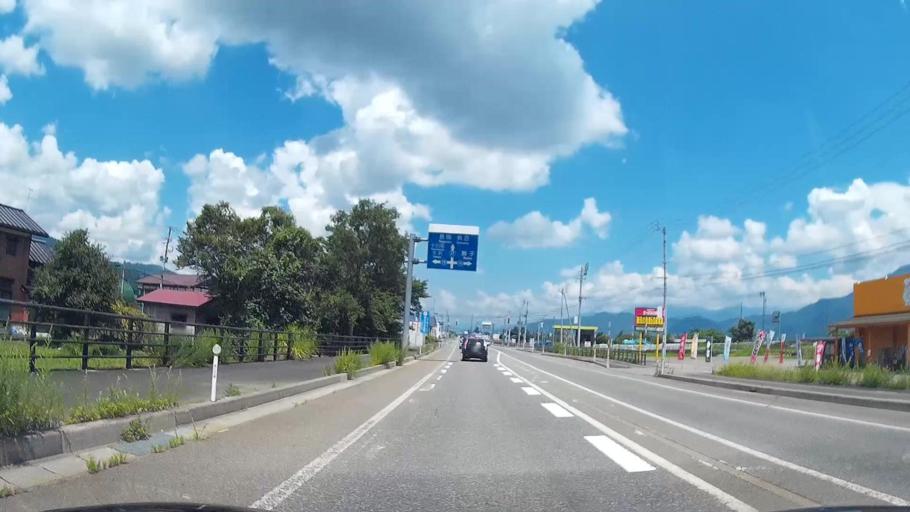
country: JP
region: Niigata
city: Shiozawa
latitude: 37.0147
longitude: 138.8273
